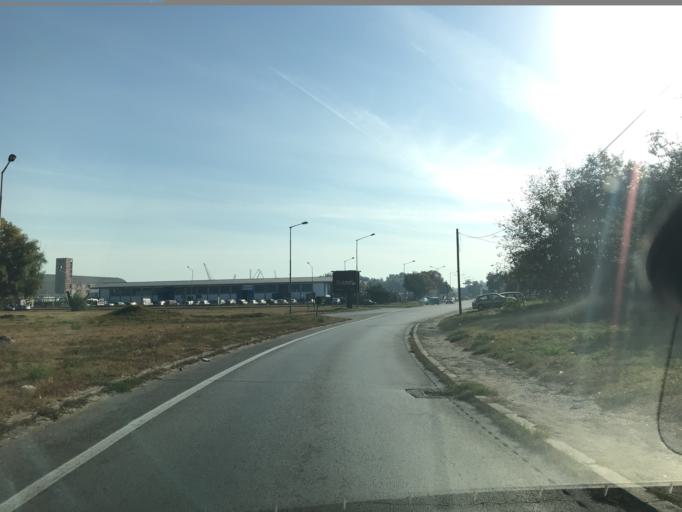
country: RS
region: Autonomna Pokrajina Vojvodina
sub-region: Juznobacki Okrug
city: Novi Sad
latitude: 45.2706
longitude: 19.8454
